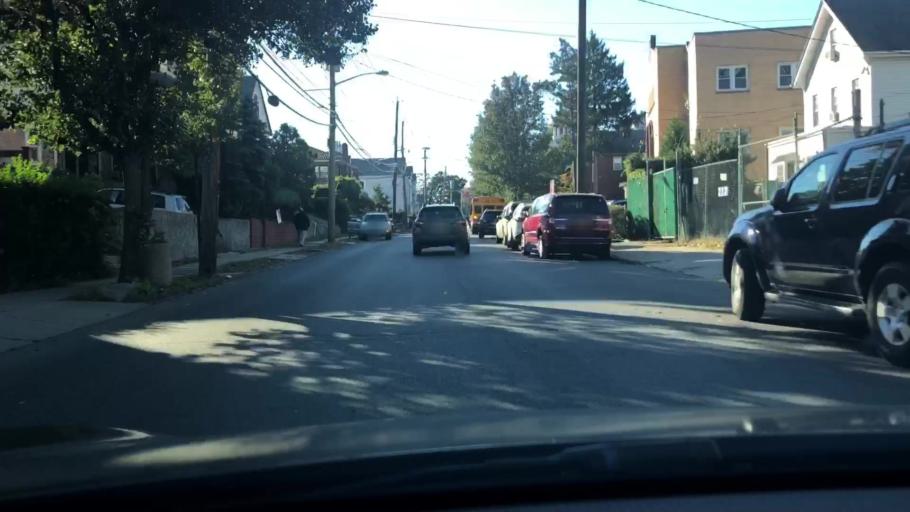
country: US
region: New York
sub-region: Westchester County
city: Pelham
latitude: 40.9093
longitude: -73.8218
